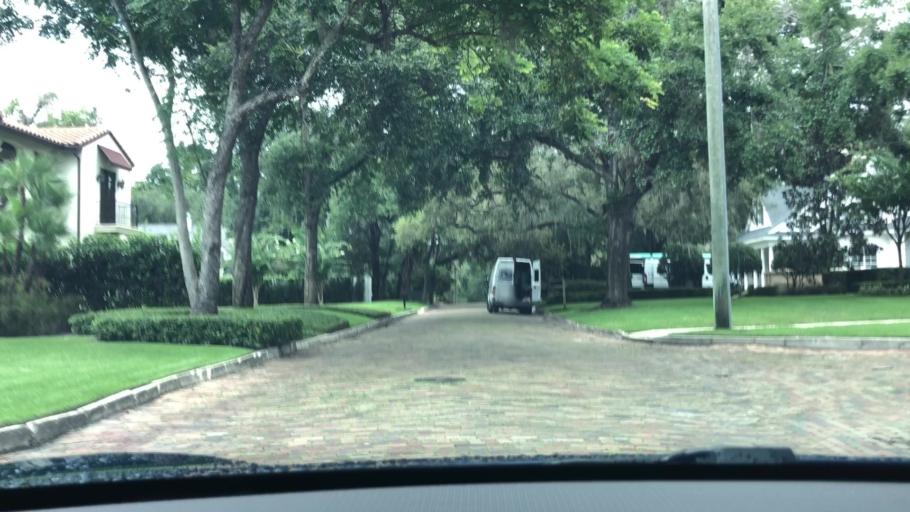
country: US
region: Florida
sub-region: Orange County
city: Winter Park
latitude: 28.5764
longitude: -81.3484
